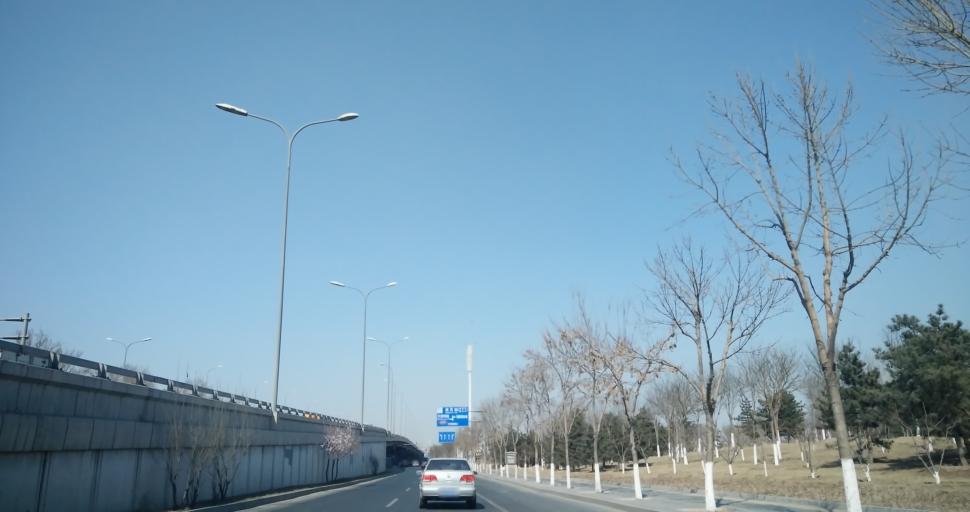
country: CN
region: Beijing
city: Jiugong
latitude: 39.7951
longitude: 116.4239
